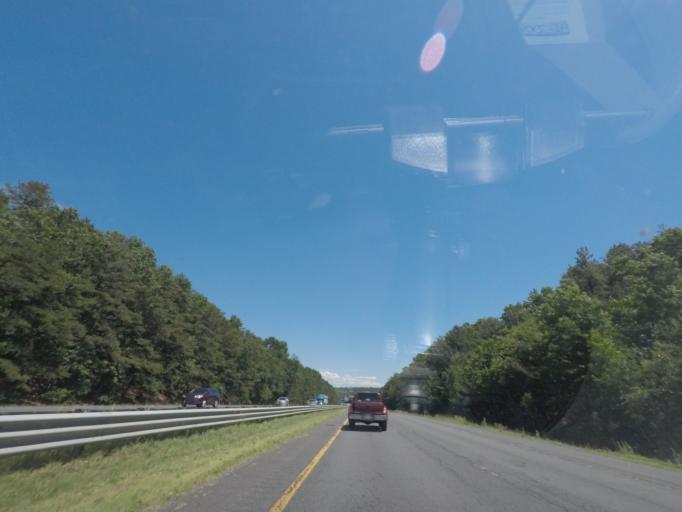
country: US
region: Massachusetts
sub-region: Hampden County
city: Westfield
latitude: 42.1418
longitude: -72.7184
